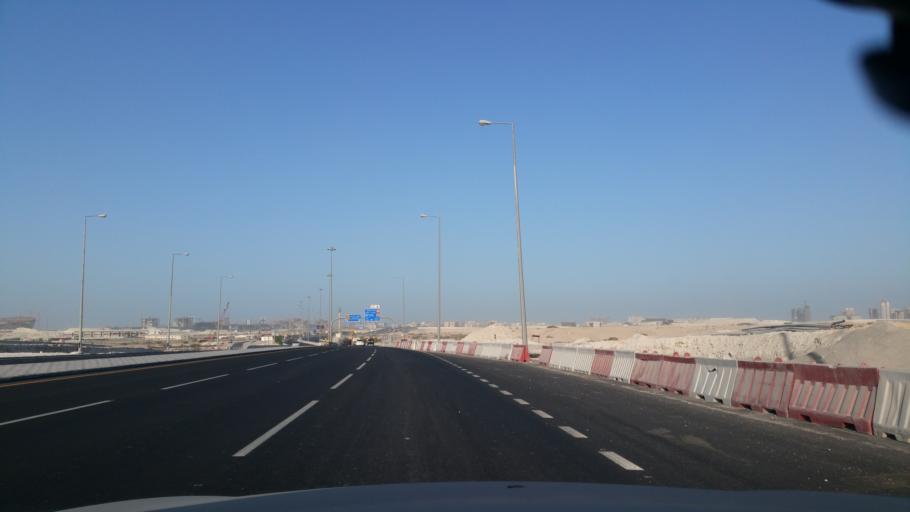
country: QA
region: Baladiyat Umm Salal
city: Umm Salal Muhammad
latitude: 25.3943
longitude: 51.4745
